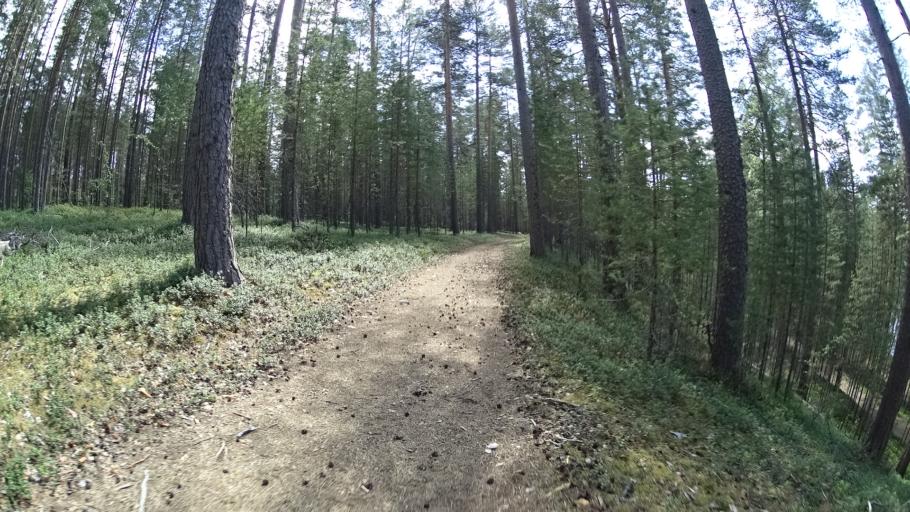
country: FI
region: Southern Savonia
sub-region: Savonlinna
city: Punkaharju
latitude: 61.7889
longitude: 29.3076
